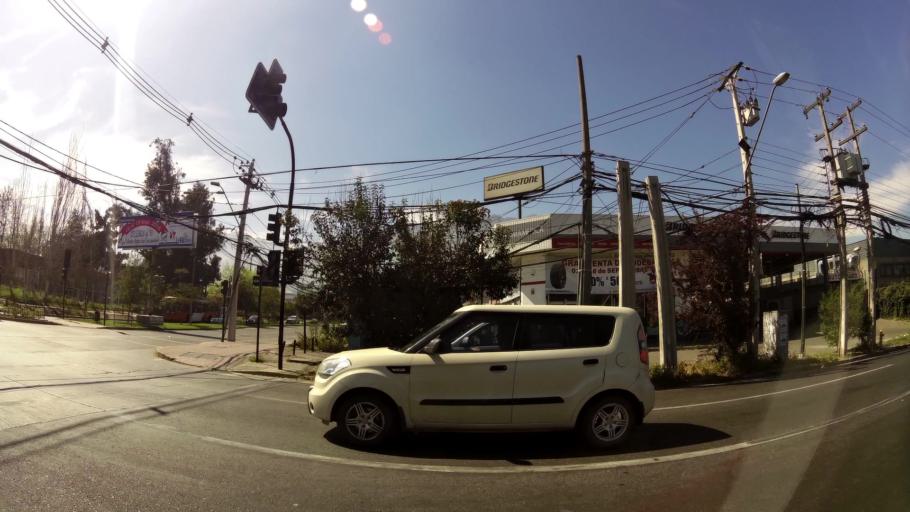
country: CL
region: Santiago Metropolitan
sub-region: Provincia de Santiago
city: Villa Presidente Frei, Nunoa, Santiago, Chile
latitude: -33.4514
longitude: -70.5437
